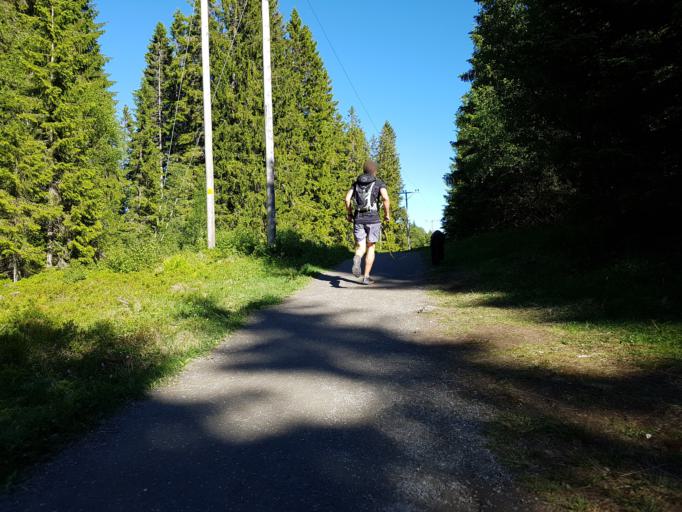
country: NO
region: Sor-Trondelag
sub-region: Trondheim
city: Trondheim
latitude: 63.4180
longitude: 10.3166
